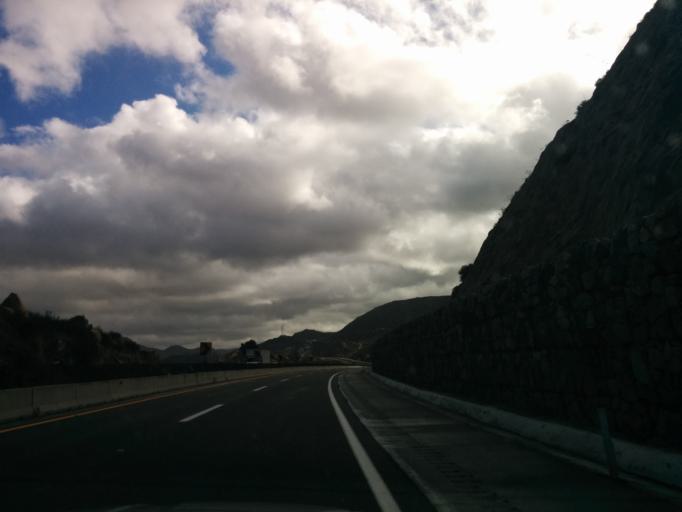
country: MX
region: Baja California
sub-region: Tecate
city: Hacienda Tecate
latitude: 32.5609
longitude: -116.5628
